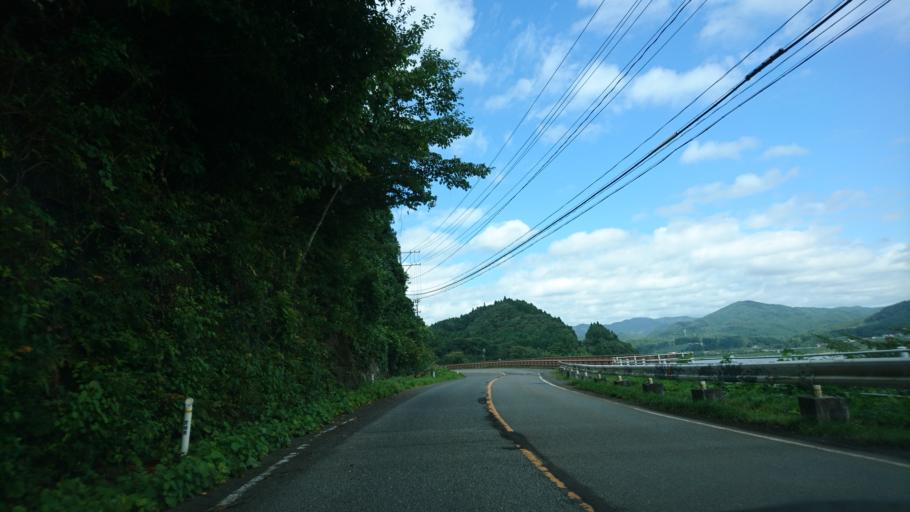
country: JP
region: Miyagi
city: Furukawa
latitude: 38.7768
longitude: 140.8545
